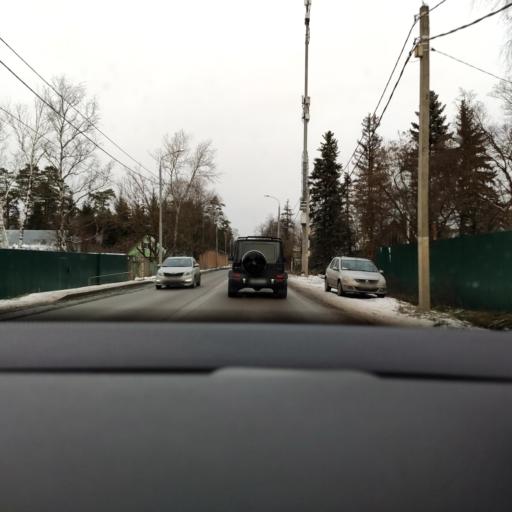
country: RU
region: Moskovskaya
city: Zhavoronki
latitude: 55.6498
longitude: 37.1008
